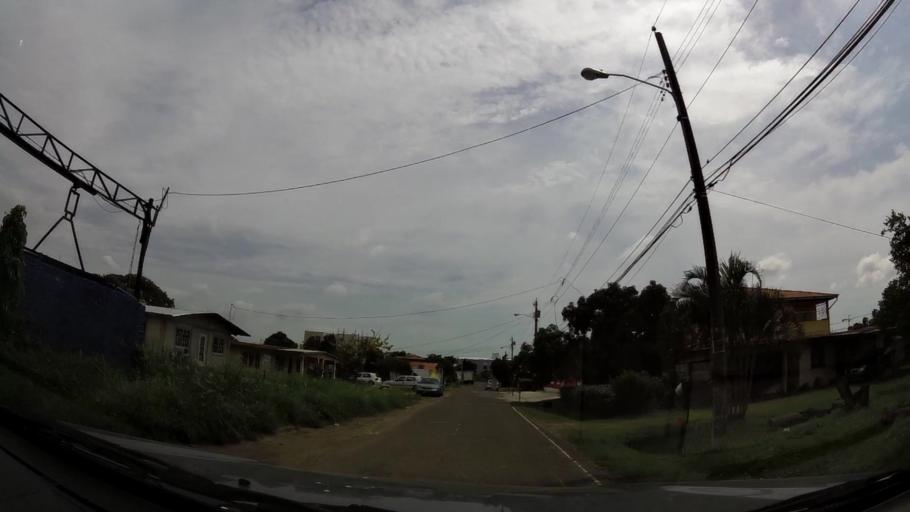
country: PA
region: Panama
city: San Miguelito
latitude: 9.0453
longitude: -79.4212
